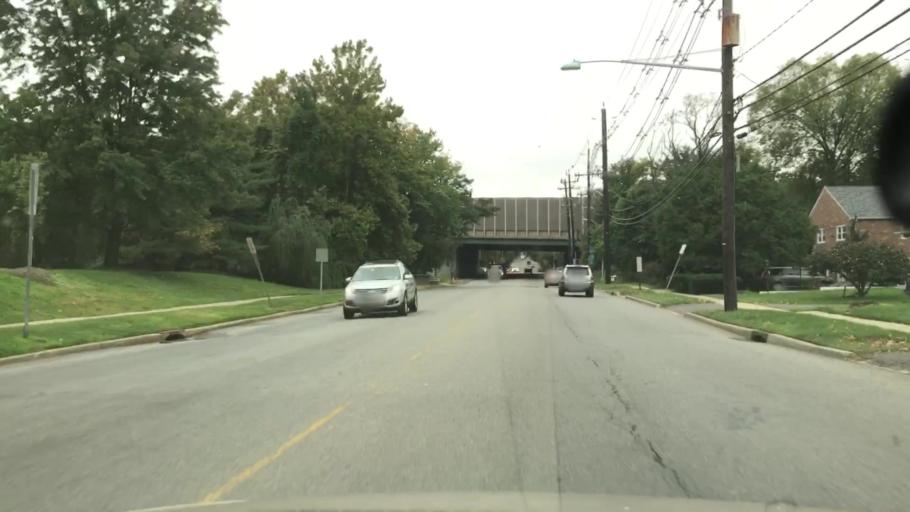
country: US
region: New Jersey
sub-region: Bergen County
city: Leonia
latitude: 40.8736
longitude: -73.9795
